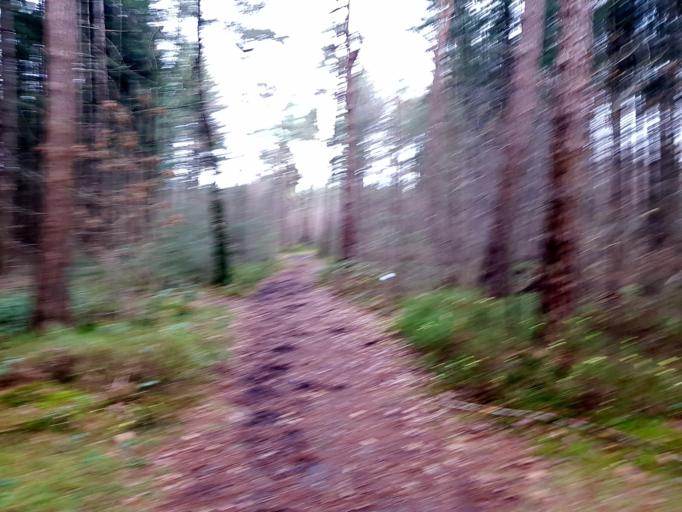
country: NL
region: Utrecht
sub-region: Gemeente Utrechtse Heuvelrug
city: Maarsbergen
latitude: 52.0348
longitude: 5.3863
